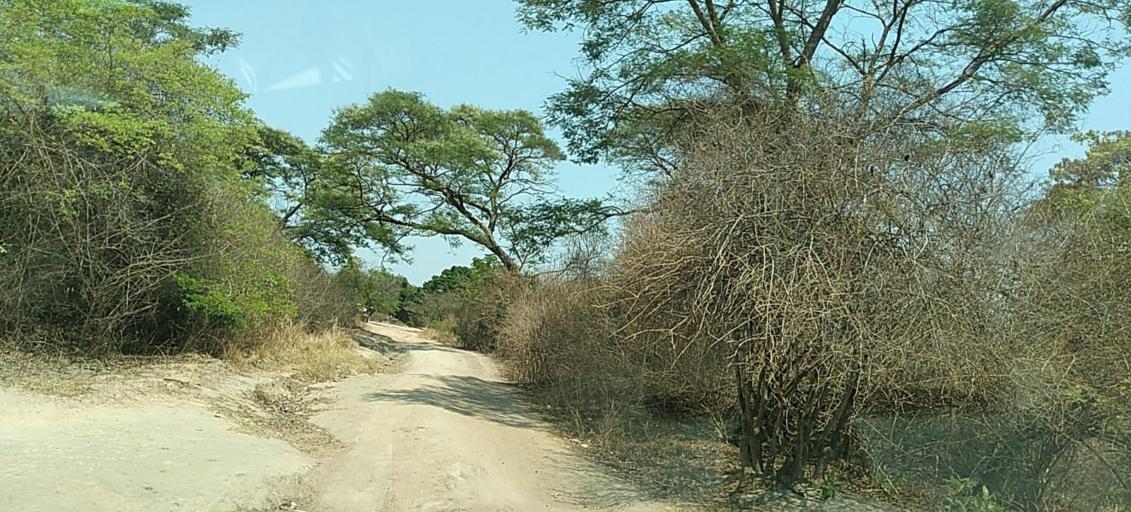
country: ZM
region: Copperbelt
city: Mpongwe
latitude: -13.8669
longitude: 27.8808
